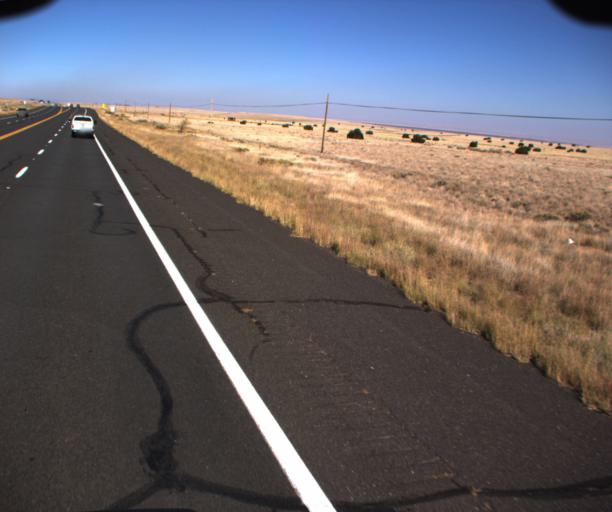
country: US
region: Arizona
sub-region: Coconino County
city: Flagstaff
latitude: 35.5717
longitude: -111.5315
